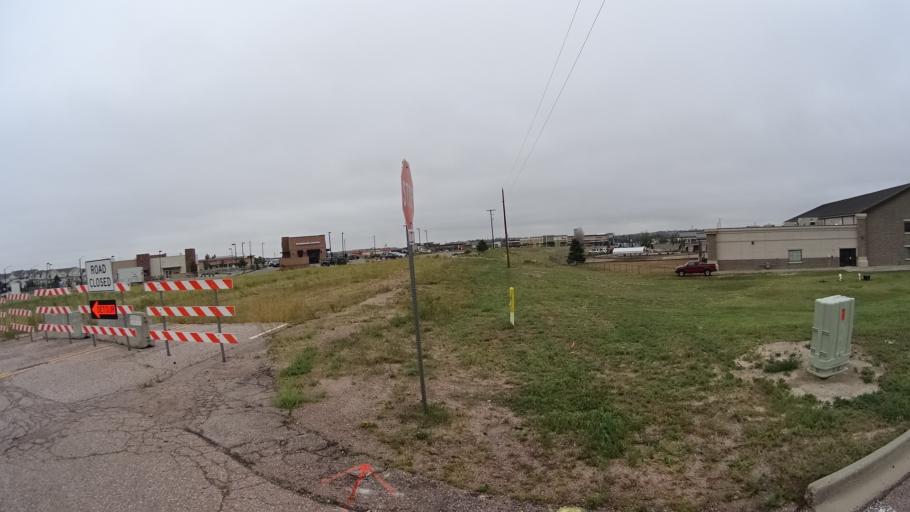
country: US
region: Colorado
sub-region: El Paso County
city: Cimarron Hills
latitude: 38.9273
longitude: -104.7158
